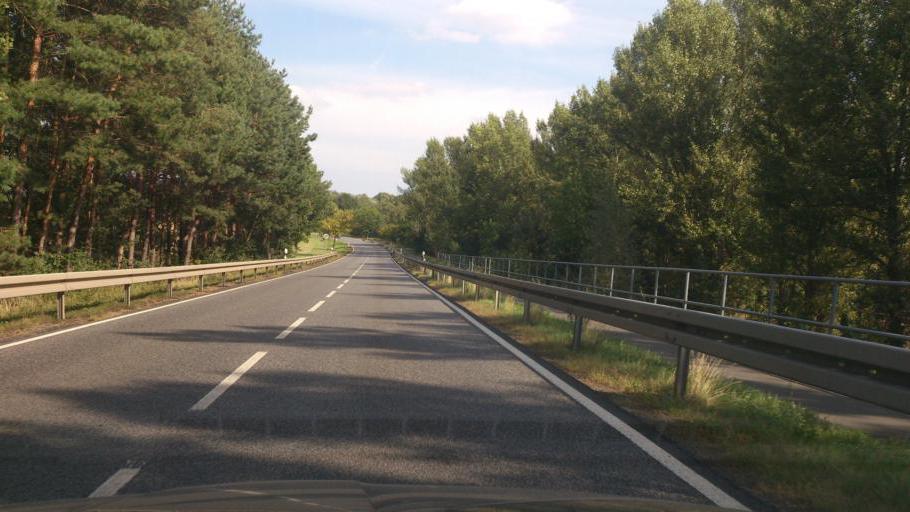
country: DE
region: Brandenburg
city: Ludwigsfelde
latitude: 52.3193
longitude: 13.2029
